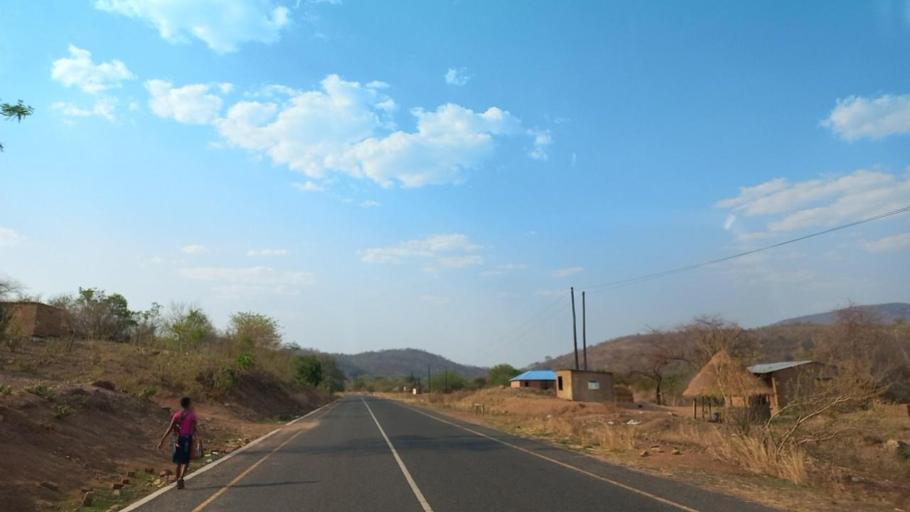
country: ZM
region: Lusaka
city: Luangwa
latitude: -14.9920
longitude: 30.2132
